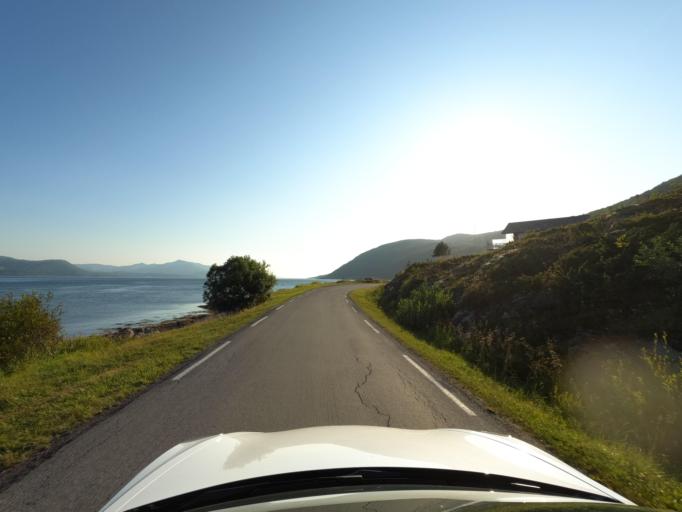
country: NO
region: Nordland
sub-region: Ballangen
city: Ballangen
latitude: 68.4676
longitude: 16.8145
